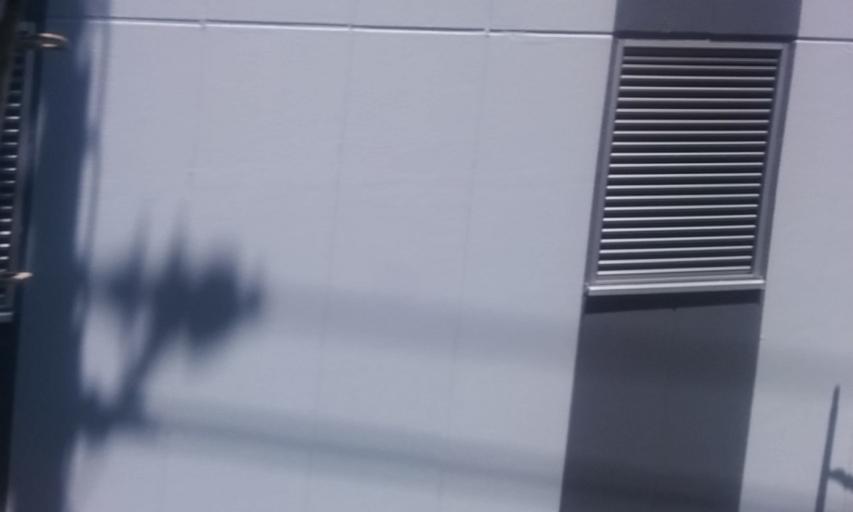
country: JP
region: Chiba
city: Chiba
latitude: 35.6114
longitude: 140.1156
